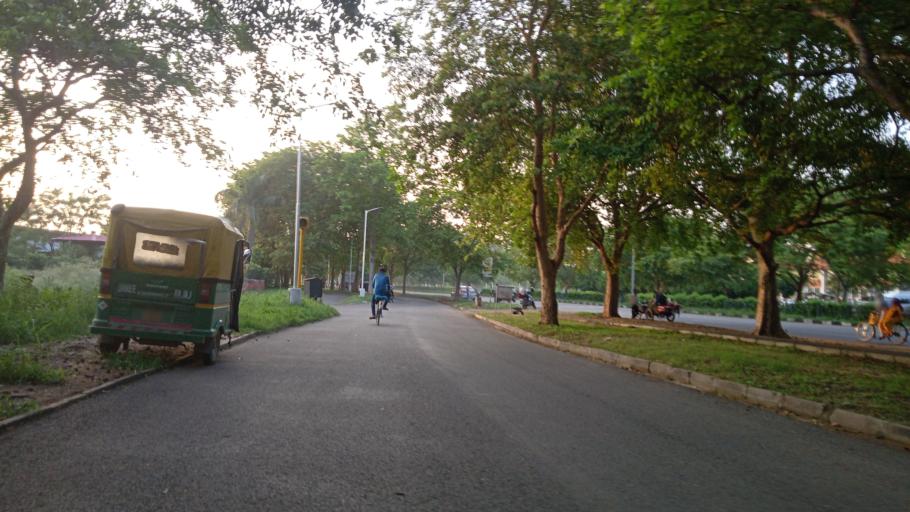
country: IN
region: Chandigarh
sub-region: Chandigarh
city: Chandigarh
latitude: 30.7475
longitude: 76.7514
